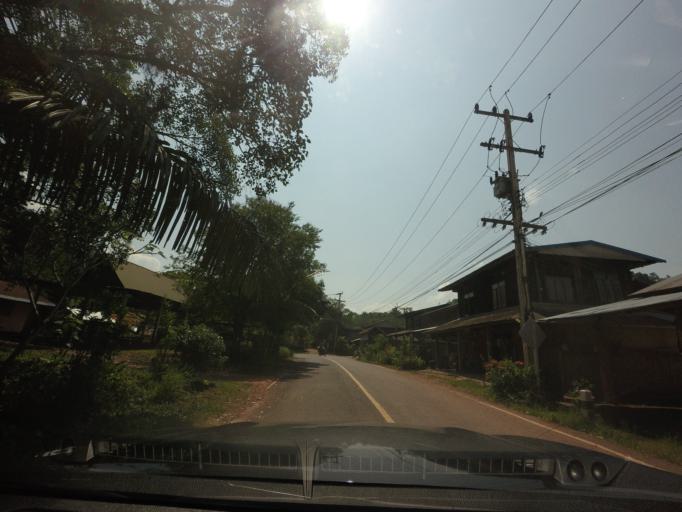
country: TH
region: Nan
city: Bo Kluea
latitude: 19.0357
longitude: 101.1711
